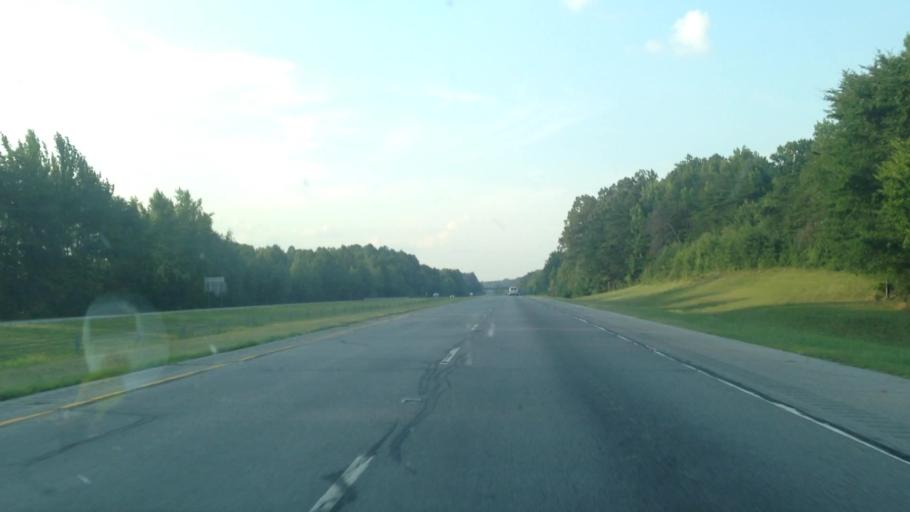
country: US
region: Virginia
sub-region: City of Danville
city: Danville
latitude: 36.4956
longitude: -79.4837
